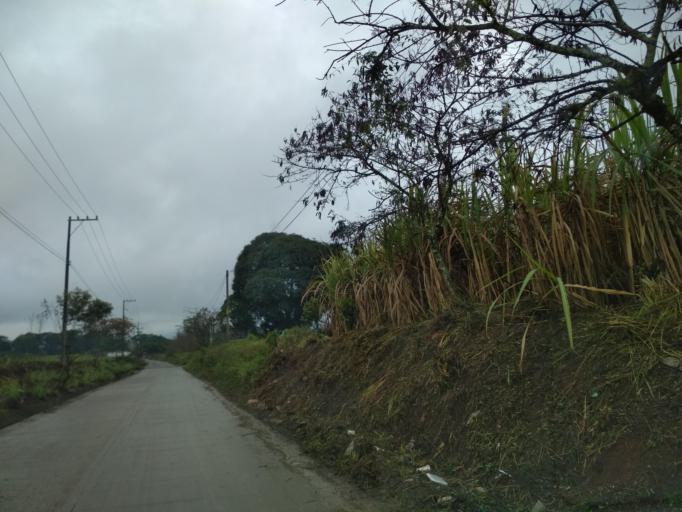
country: MX
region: Veracruz
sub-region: Amatlan de los Reyes
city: Centro de Readaptacion Social
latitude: 18.8379
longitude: -96.9394
